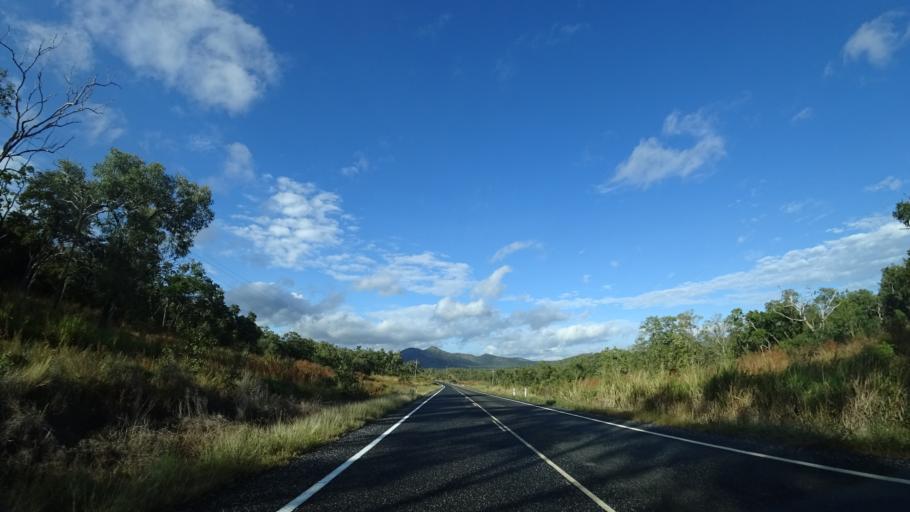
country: AU
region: Queensland
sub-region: Cook
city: Cooktown
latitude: -15.6054
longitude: 145.2223
